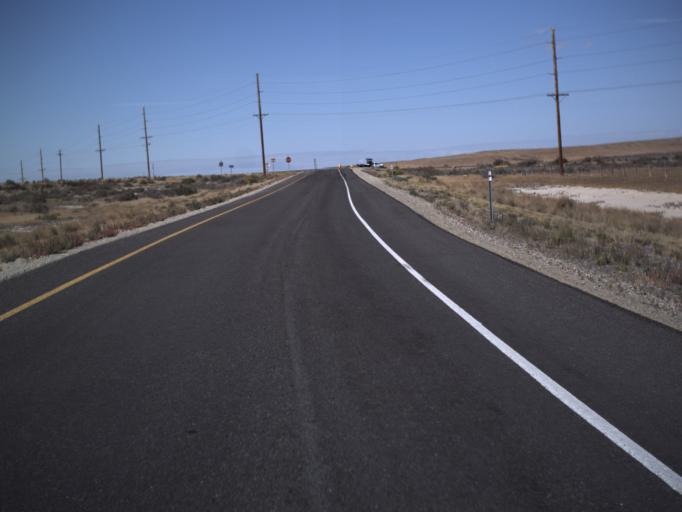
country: US
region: Utah
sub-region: Tooele County
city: Grantsville
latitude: 40.7335
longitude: -113.1111
